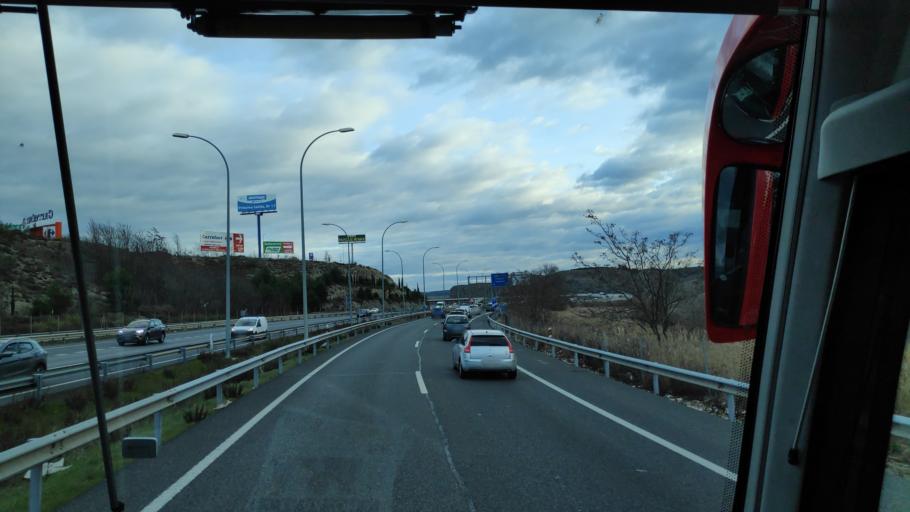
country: ES
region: Madrid
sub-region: Provincia de Madrid
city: Vaciamadrid
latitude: 40.3424
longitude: -3.5394
